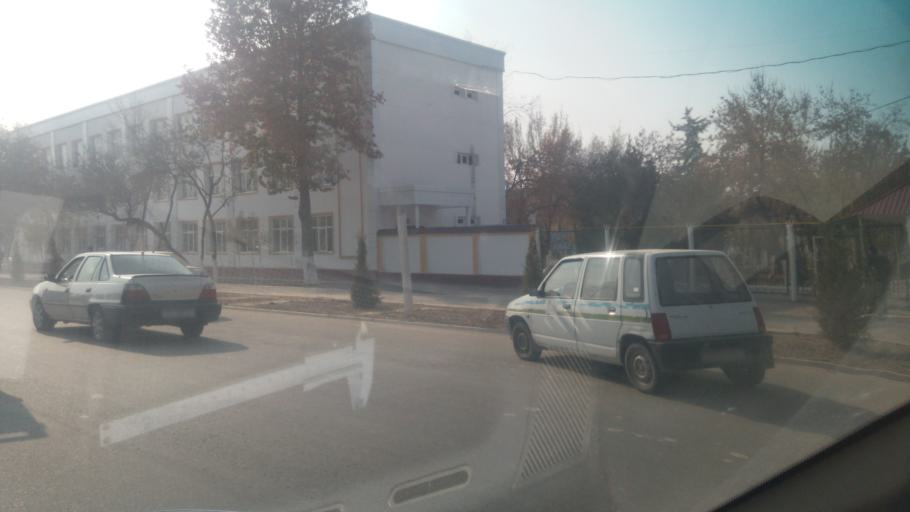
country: UZ
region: Sirdaryo
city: Guliston
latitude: 40.5112
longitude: 68.7706
